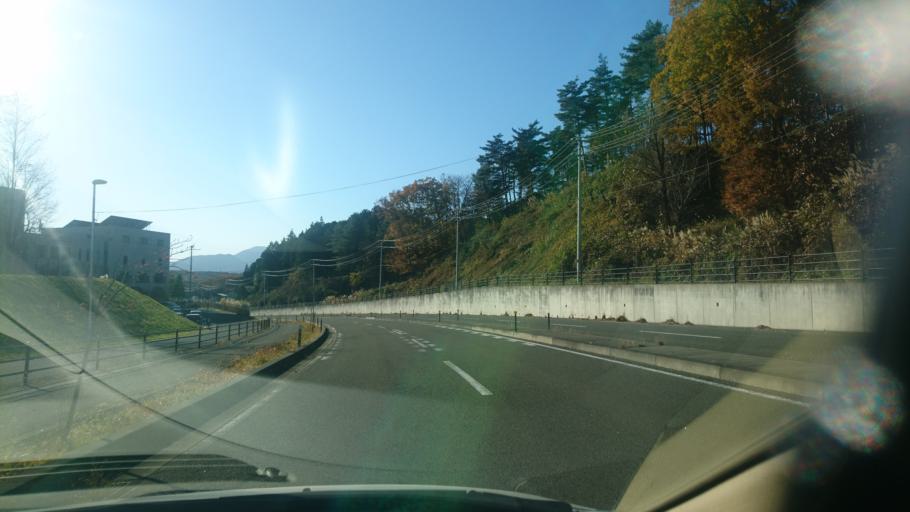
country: JP
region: Miyagi
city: Tomiya
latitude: 38.4680
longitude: 140.8810
